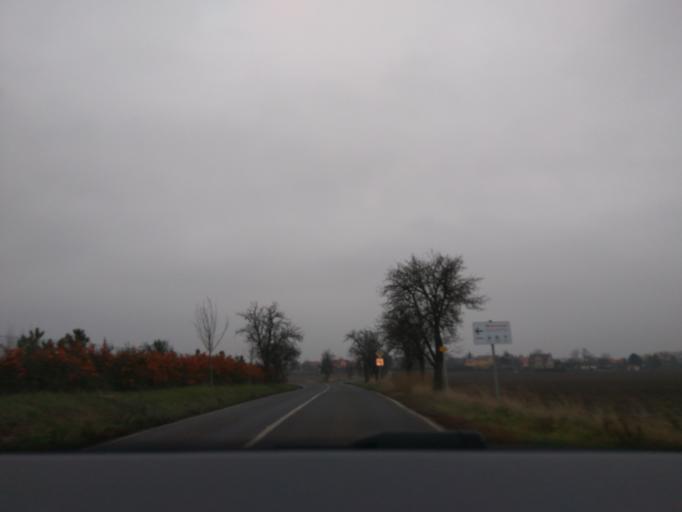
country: CZ
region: Praha
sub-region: Praha 19
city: Kbely
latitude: 50.1503
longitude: 14.5431
